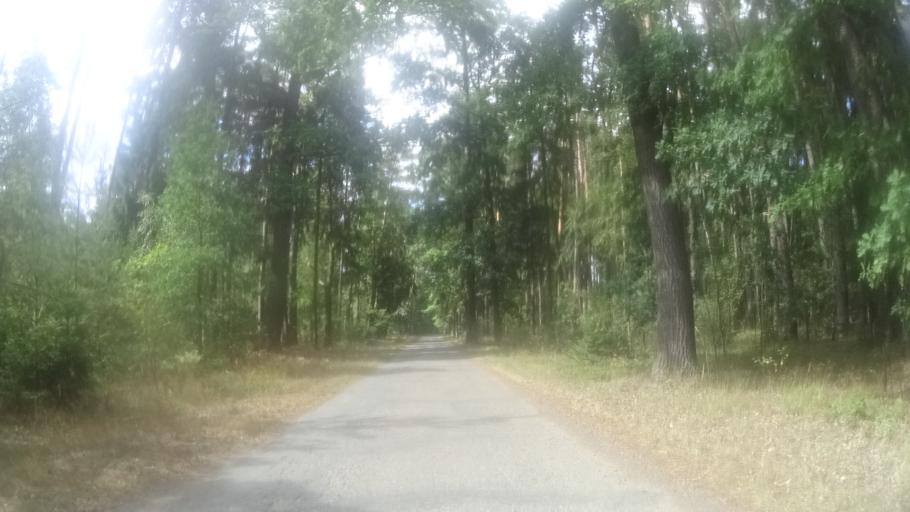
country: CZ
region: Pardubicky
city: Horni Jeleni
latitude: 50.0513
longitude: 16.1543
